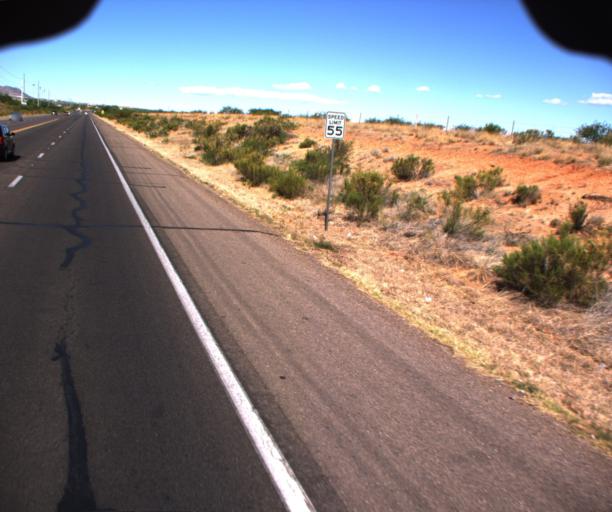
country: US
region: Arizona
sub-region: Cochise County
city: Sierra Vista
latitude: 31.5695
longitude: -110.2950
